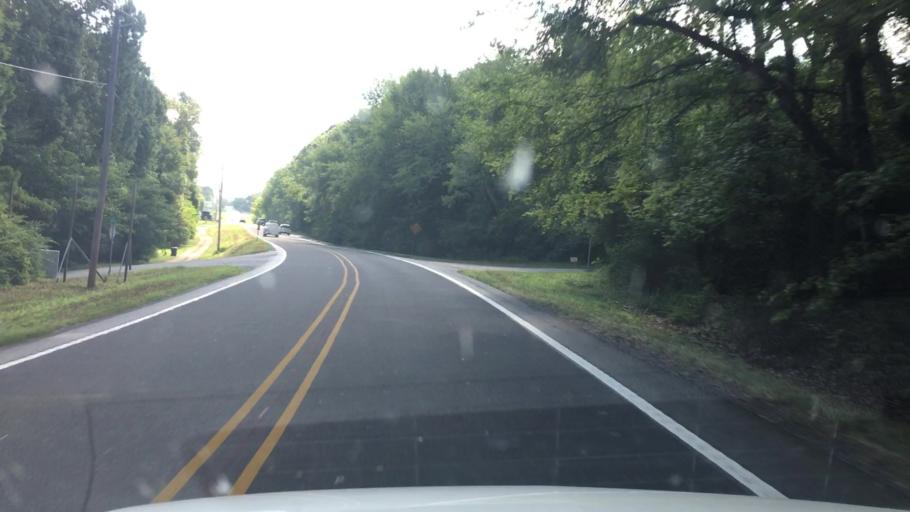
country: US
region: Arkansas
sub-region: Garland County
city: Piney
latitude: 34.5096
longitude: -93.1675
